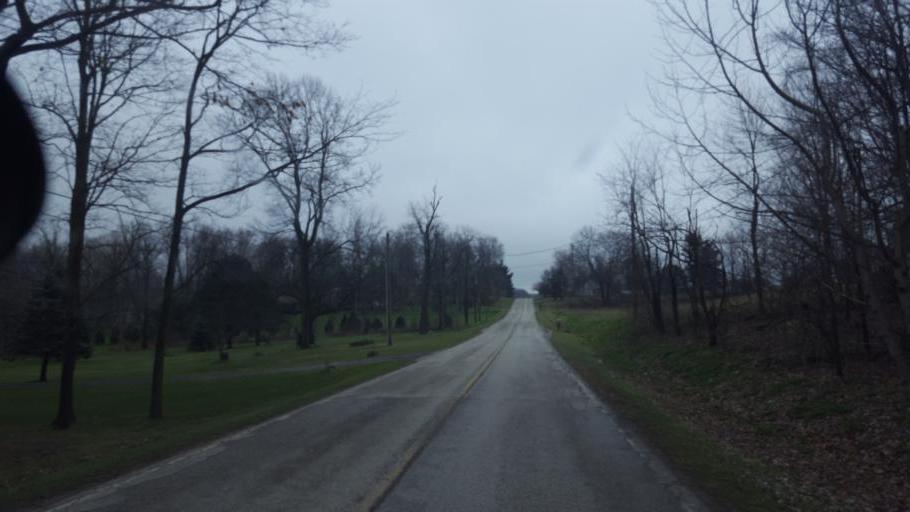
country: US
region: Ohio
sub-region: Richland County
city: Lexington
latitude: 40.6832
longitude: -82.5209
